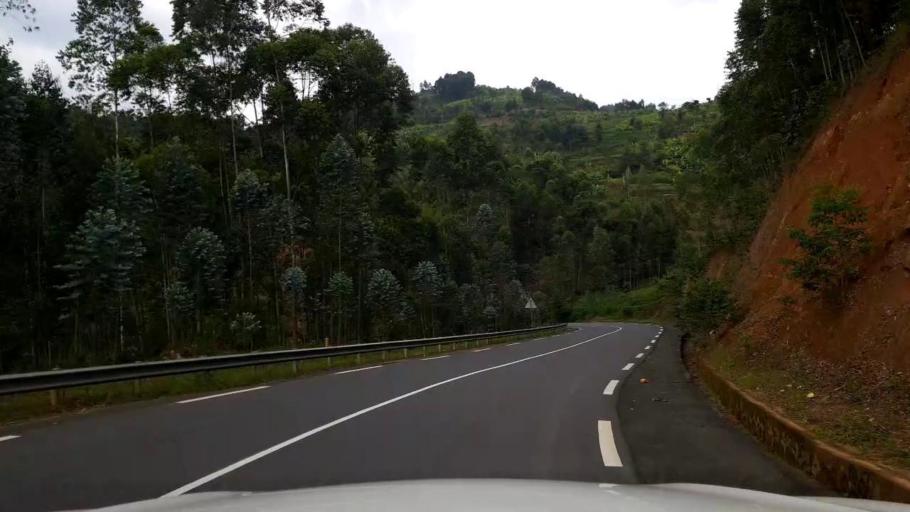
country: RW
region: Western Province
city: Kibuye
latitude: -1.9066
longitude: 29.3631
